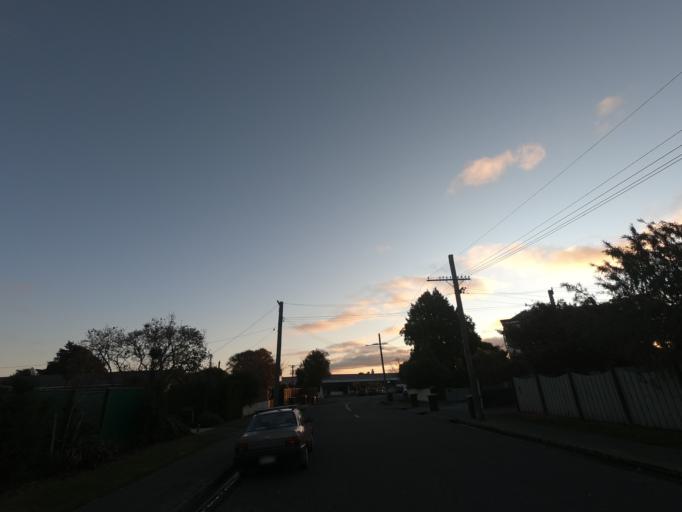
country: NZ
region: Canterbury
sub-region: Selwyn District
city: Prebbleton
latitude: -43.5753
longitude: 172.5616
